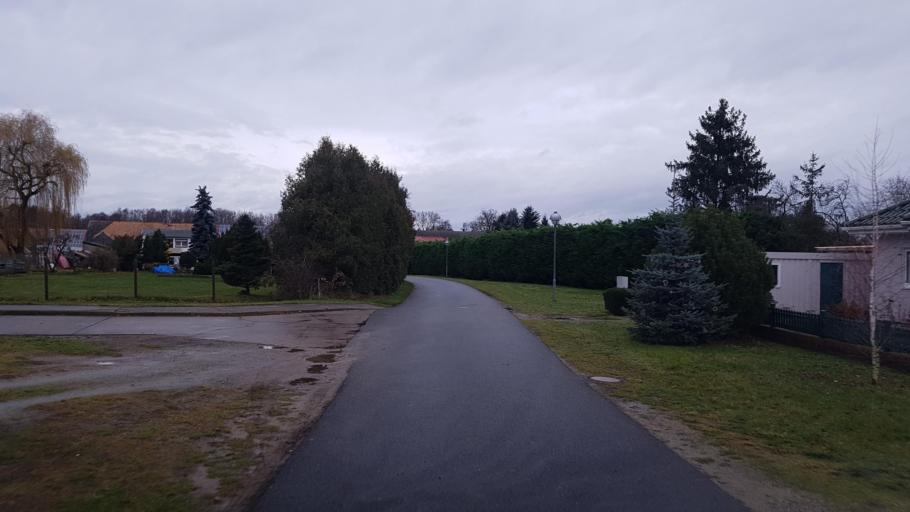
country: DE
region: Brandenburg
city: Tauche
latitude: 52.0822
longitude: 14.1689
